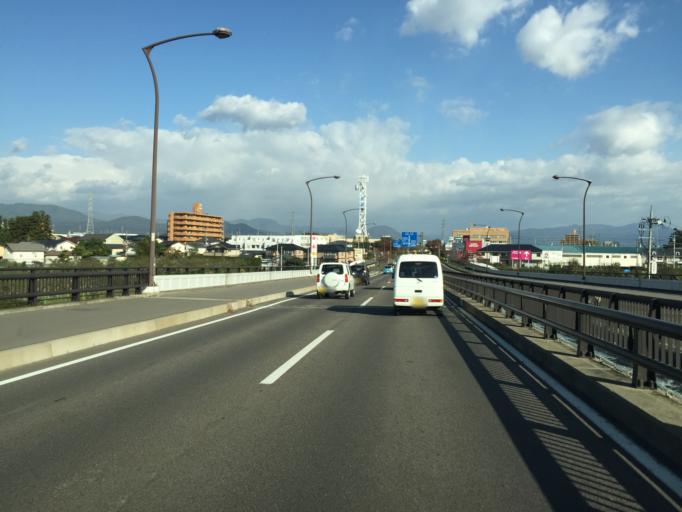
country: JP
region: Fukushima
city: Fukushima-shi
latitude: 37.7552
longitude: 140.4353
